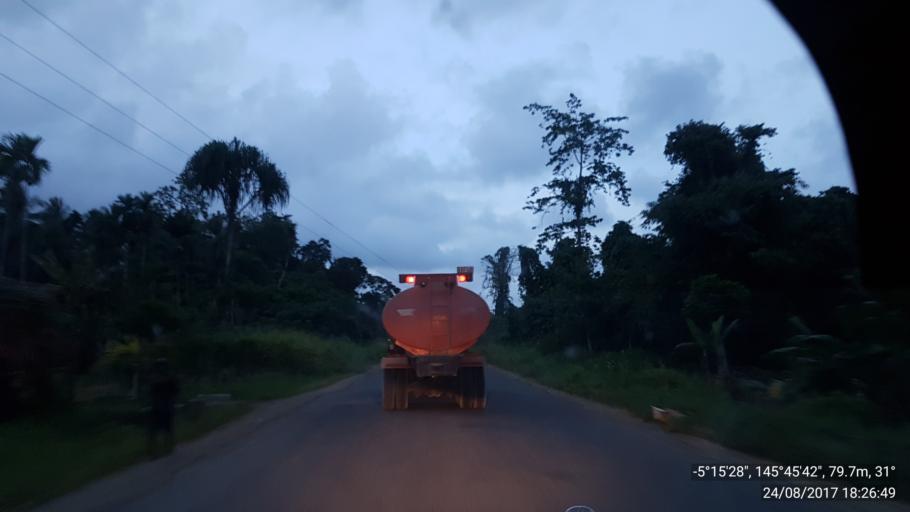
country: PG
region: Madang
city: Madang
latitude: -5.2581
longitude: 145.7617
